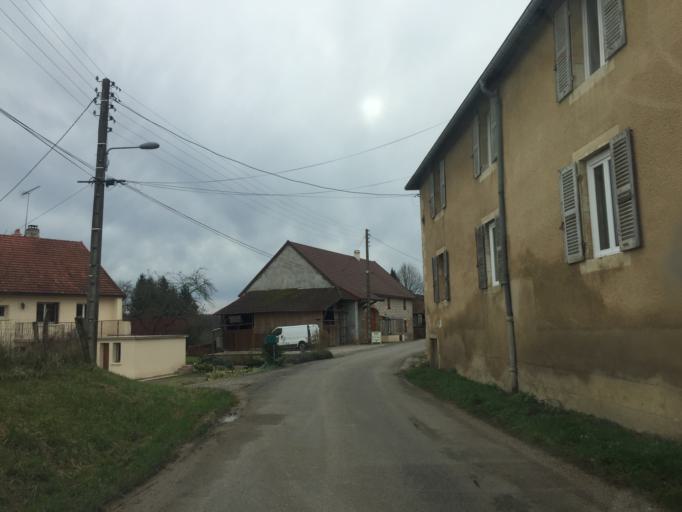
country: FR
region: Franche-Comte
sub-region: Departement du Jura
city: Mont-sous-Vaudrey
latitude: 46.8704
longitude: 5.5226
